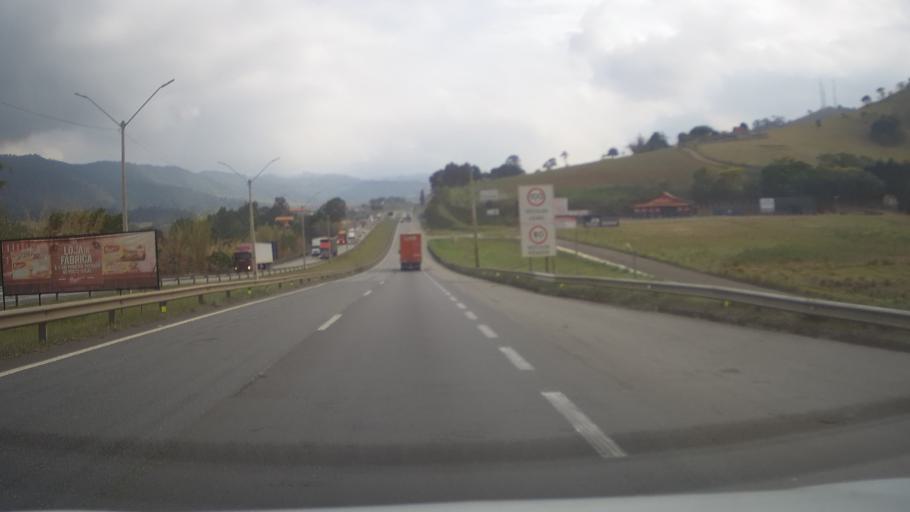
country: BR
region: Minas Gerais
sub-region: Extrema
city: Extrema
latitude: -22.9055
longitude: -46.4225
